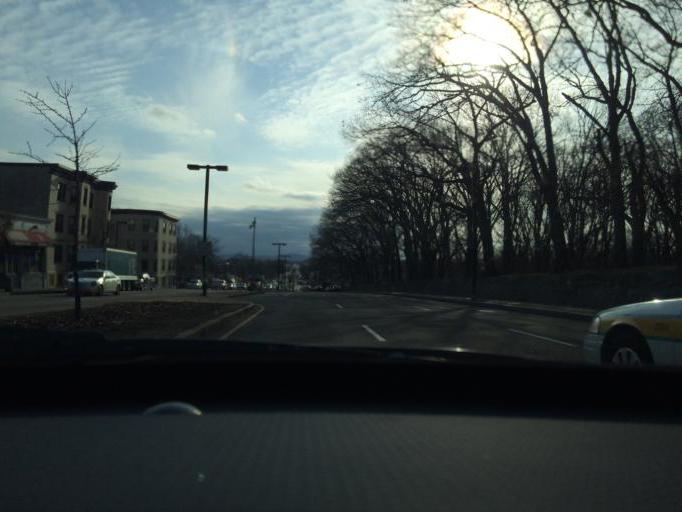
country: US
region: Massachusetts
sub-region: Suffolk County
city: Jamaica Plain
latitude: 42.3004
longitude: -71.0862
